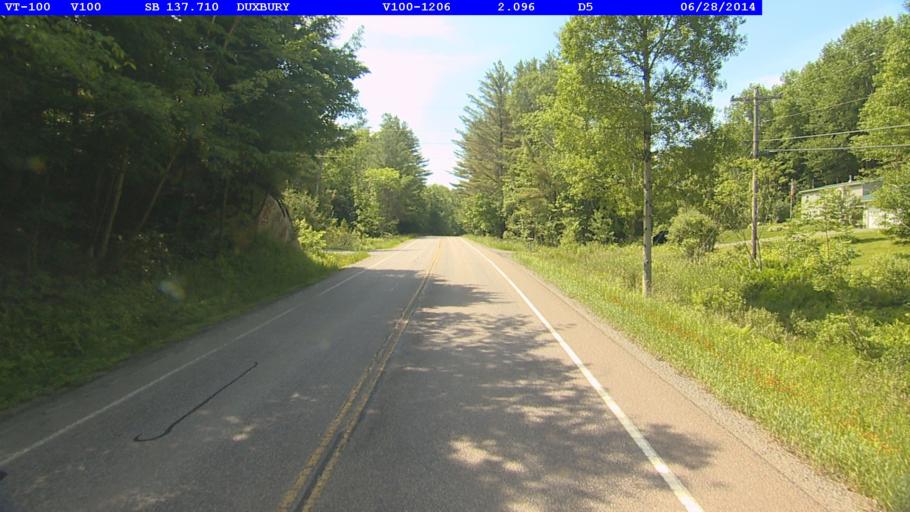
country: US
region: Vermont
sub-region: Washington County
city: Waterbury
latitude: 44.2760
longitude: -72.7846
